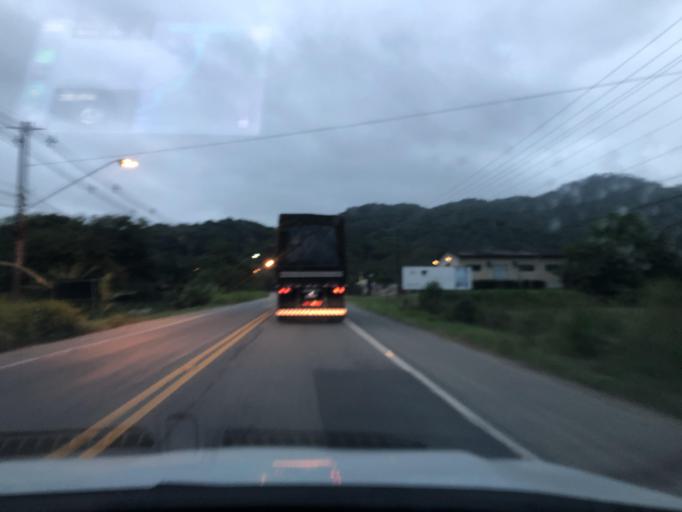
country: BR
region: Santa Catarina
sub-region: Pomerode
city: Pomerode
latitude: -26.7589
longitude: -49.0741
